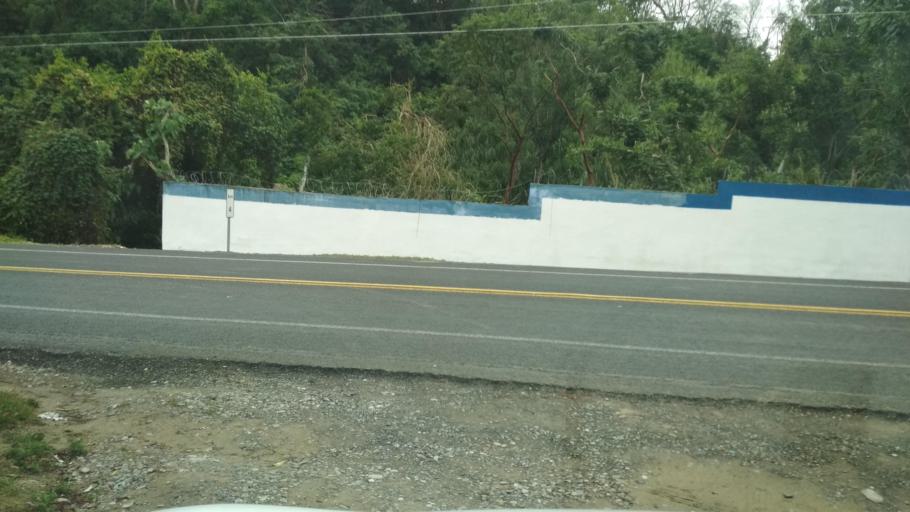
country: MX
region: Veracruz
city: Papantla de Olarte
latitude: 20.4642
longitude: -97.3081
